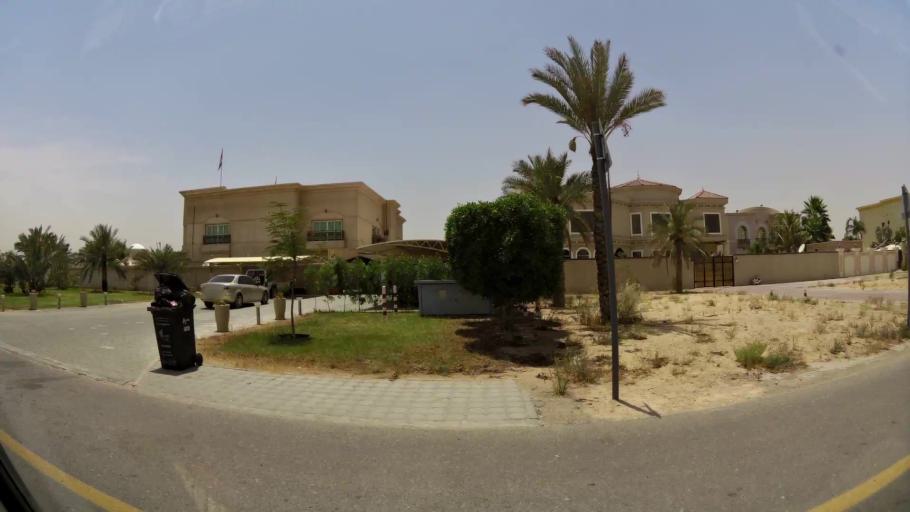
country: AE
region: Ash Shariqah
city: Sharjah
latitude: 25.2431
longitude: 55.4677
